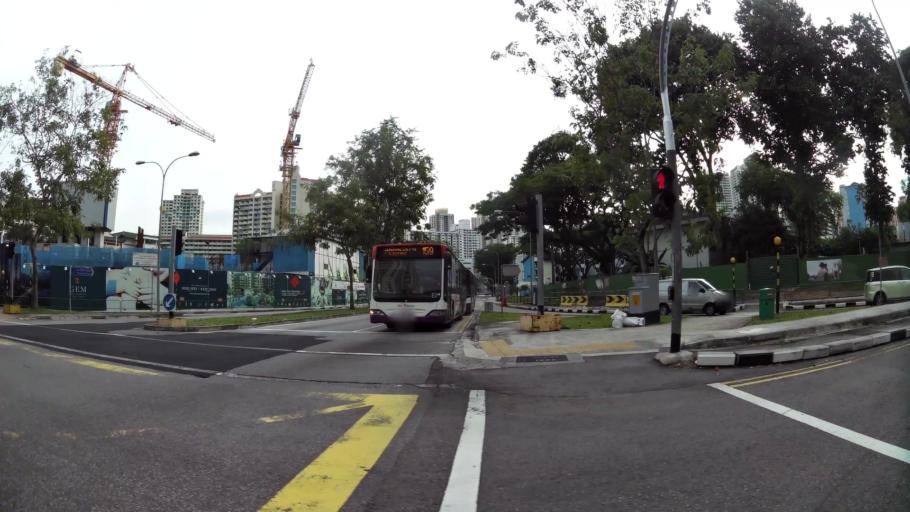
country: SG
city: Singapore
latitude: 1.3400
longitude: 103.8510
